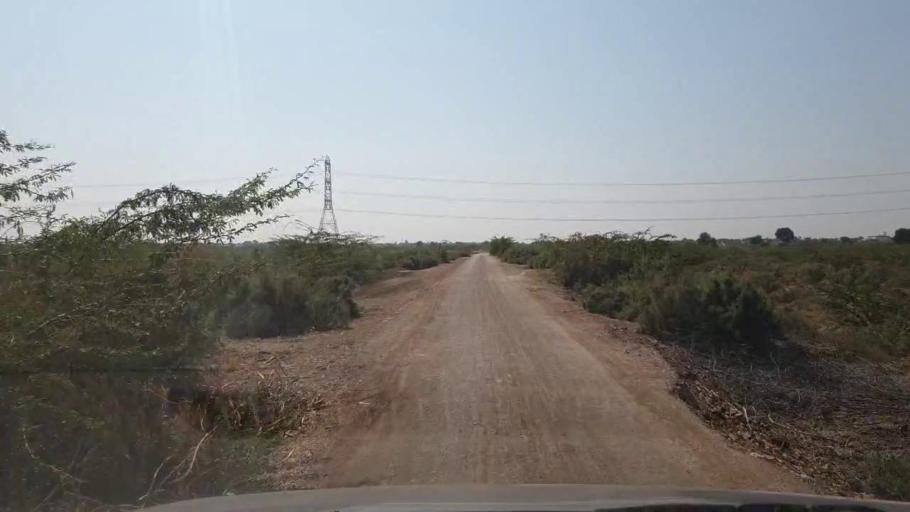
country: PK
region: Sindh
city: Digri
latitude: 25.1885
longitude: 69.2216
